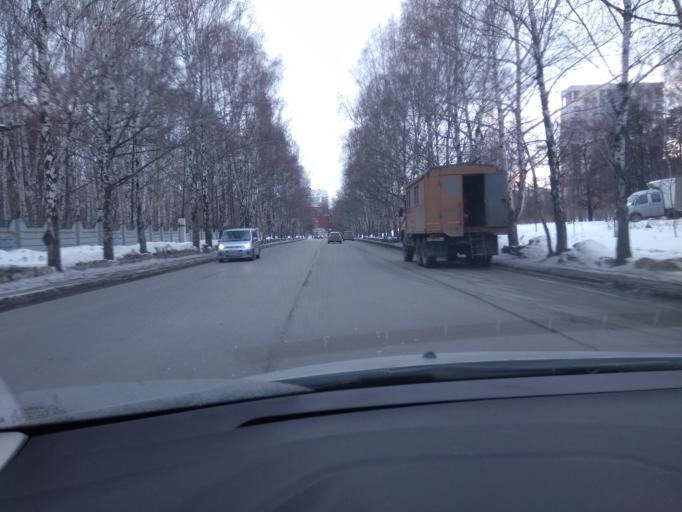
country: RU
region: Sverdlovsk
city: Yekaterinburg
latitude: 56.8500
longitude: 60.6382
